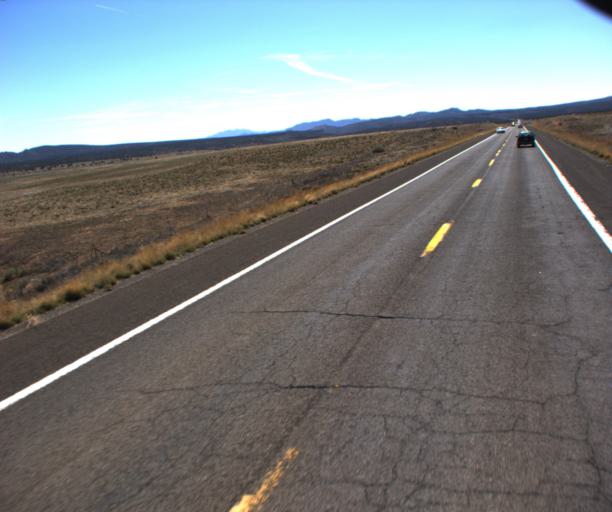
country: US
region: Arizona
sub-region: Mohave County
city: Peach Springs
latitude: 35.4742
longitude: -113.5853
